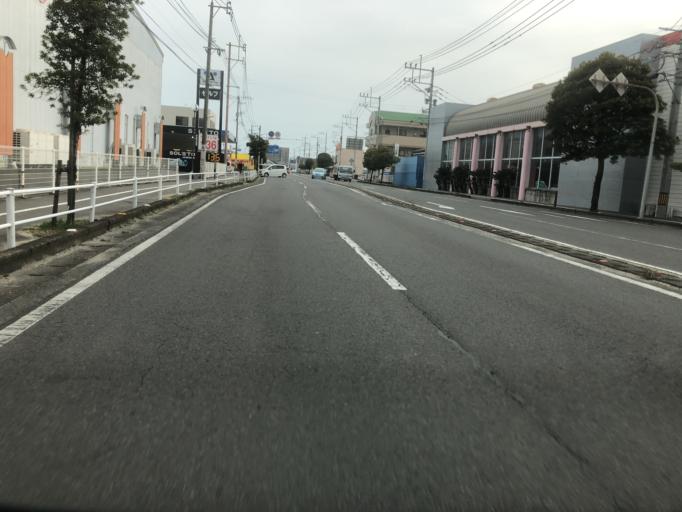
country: JP
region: Saga Prefecture
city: Saga-shi
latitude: 33.2640
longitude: 130.2723
